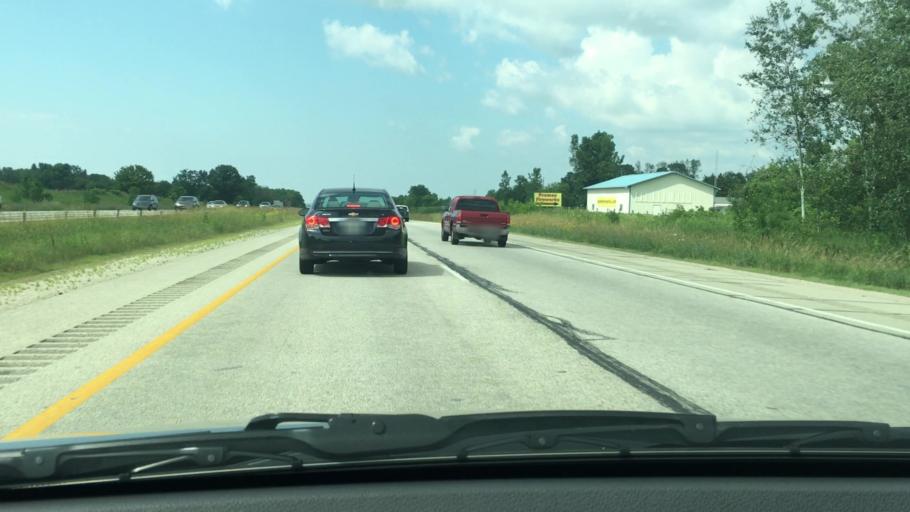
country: US
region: Wisconsin
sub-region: Fond du Lac County
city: Fond du Lac
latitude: 43.7049
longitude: -88.4422
